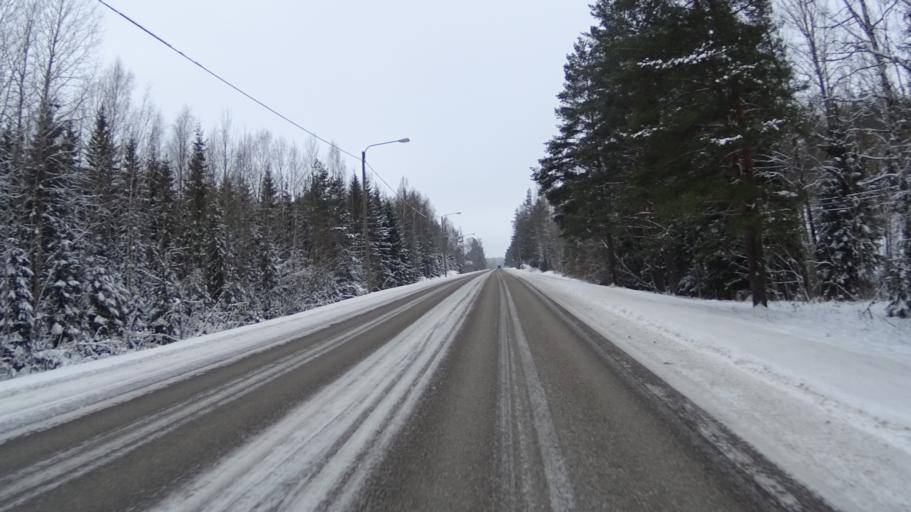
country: FI
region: Uusimaa
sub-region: Helsinki
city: Vihti
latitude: 60.3476
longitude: 24.1904
